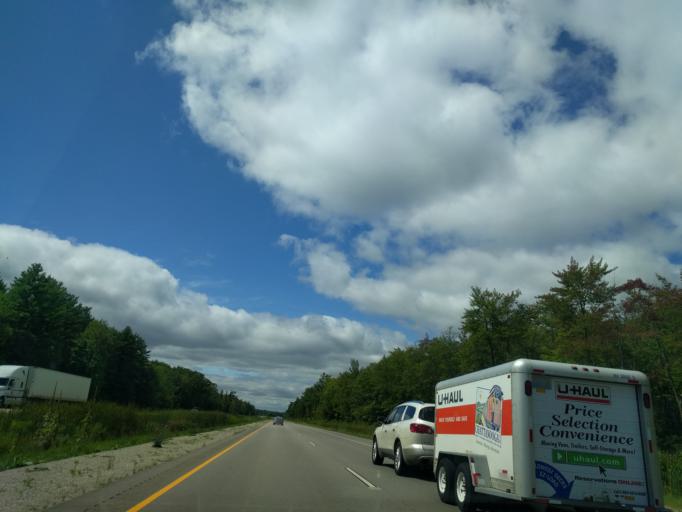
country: US
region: Wisconsin
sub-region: Oconto County
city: Oconto
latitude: 44.8100
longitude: -87.9618
